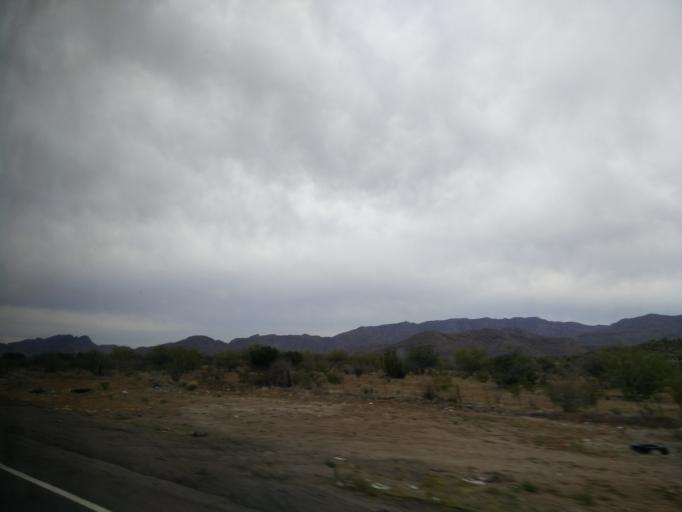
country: MX
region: Sonora
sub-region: Hermosillo
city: Miguel Aleman (La Doce)
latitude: 28.5318
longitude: -111.0454
